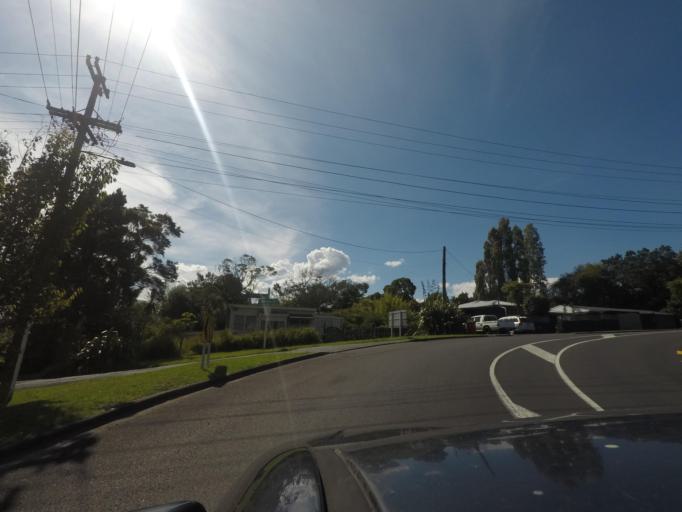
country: NZ
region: Auckland
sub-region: Auckland
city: Waitakere
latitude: -36.9236
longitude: 174.6581
